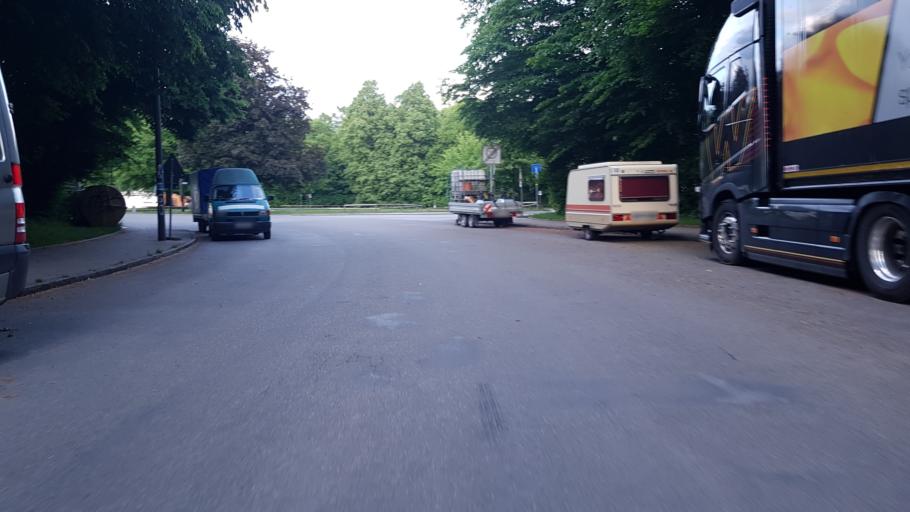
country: DE
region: Bavaria
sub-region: Upper Bavaria
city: Neuried
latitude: 48.1028
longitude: 11.4873
